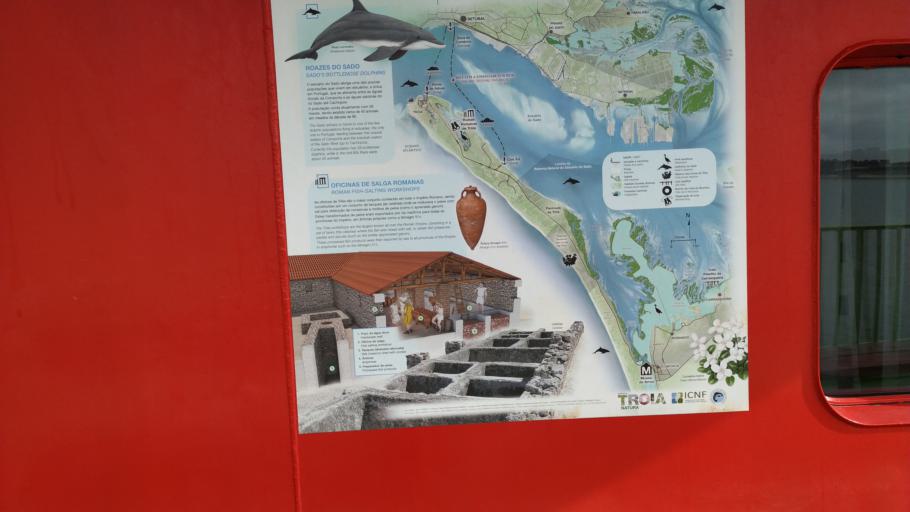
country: PT
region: Setubal
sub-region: Setubal
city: Setubal
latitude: 38.4933
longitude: -8.8838
